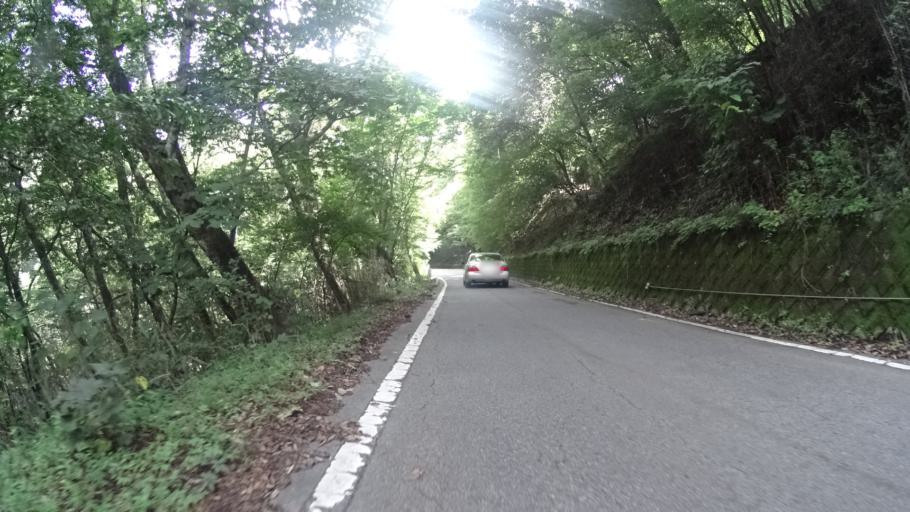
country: JP
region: Yamanashi
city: Enzan
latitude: 35.7956
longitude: 138.6835
